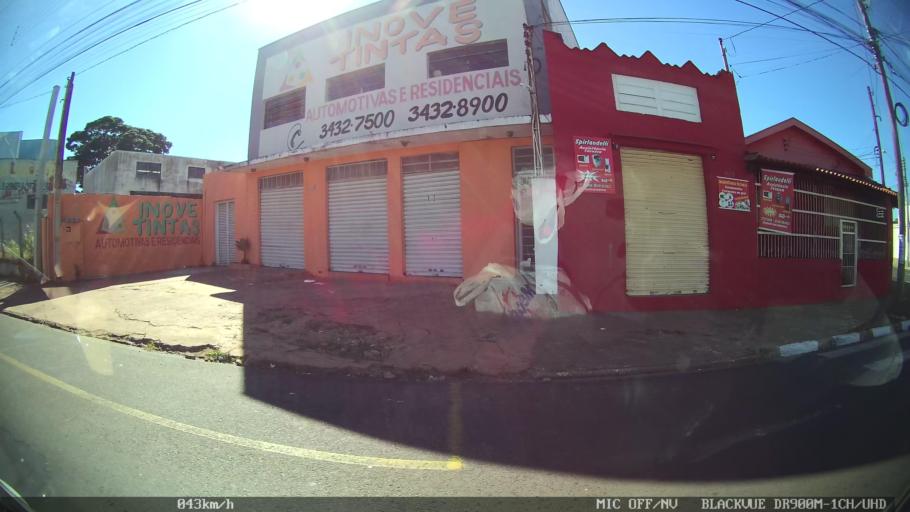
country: BR
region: Sao Paulo
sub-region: Franca
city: Franca
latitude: -20.5323
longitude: -47.3663
